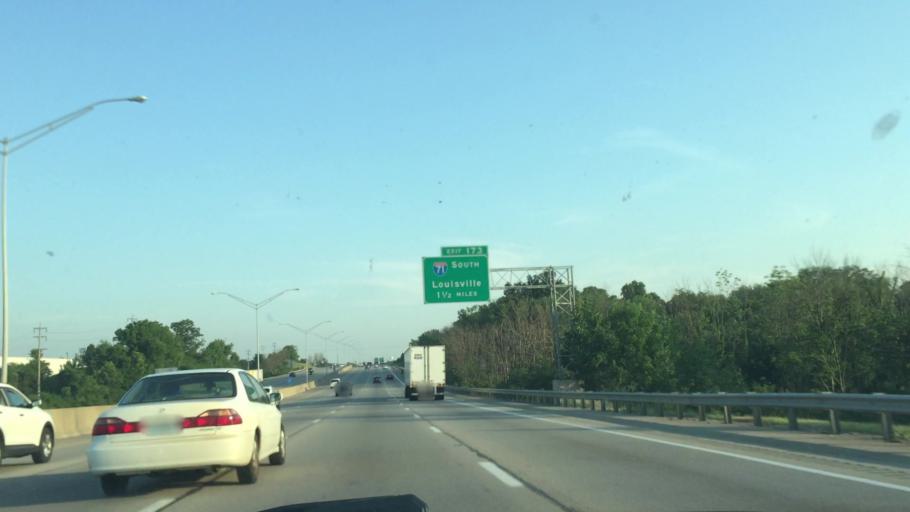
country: US
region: Kentucky
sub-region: Boone County
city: Walton
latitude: 38.9033
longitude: -84.6278
